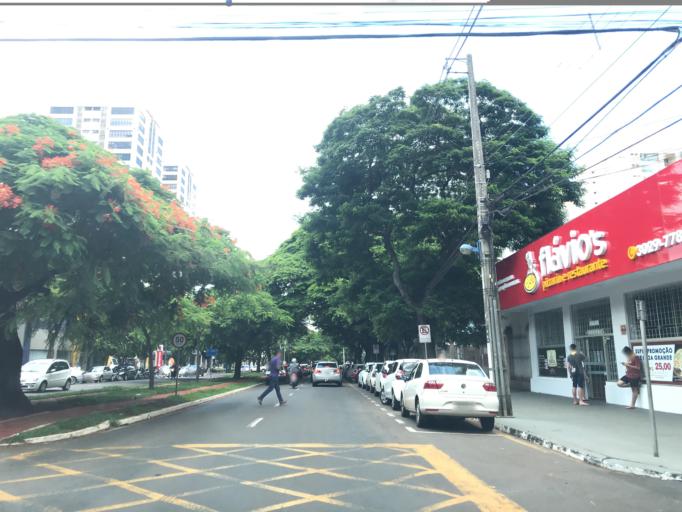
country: BR
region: Parana
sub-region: Maringa
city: Maringa
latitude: -23.4169
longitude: -51.9270
